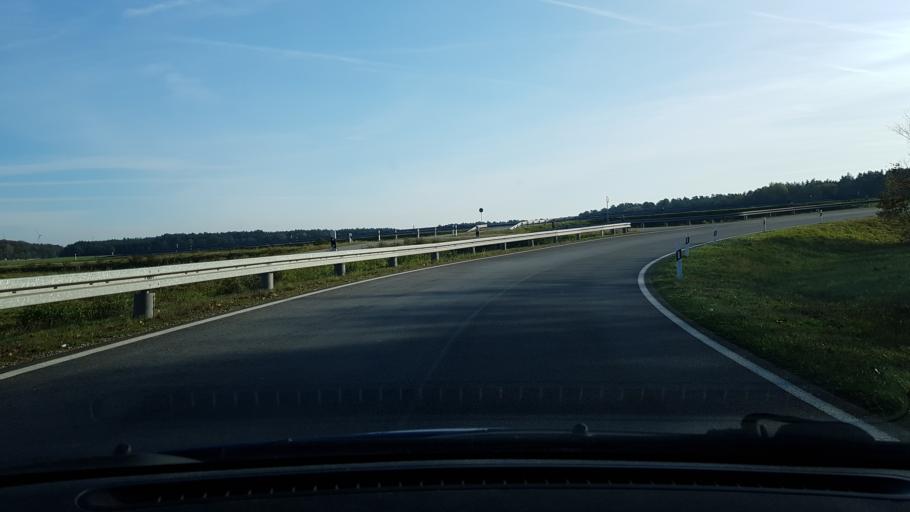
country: DE
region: Mecklenburg-Vorpommern
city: Stralendorf
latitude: 53.4854
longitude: 11.2723
